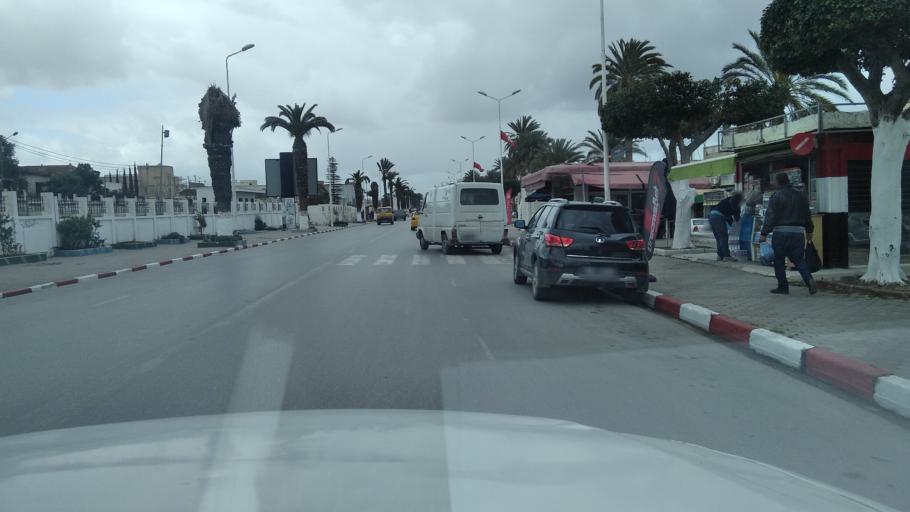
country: TN
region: Bin 'Arus
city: Ben Arous
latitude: 36.7525
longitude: 10.2238
